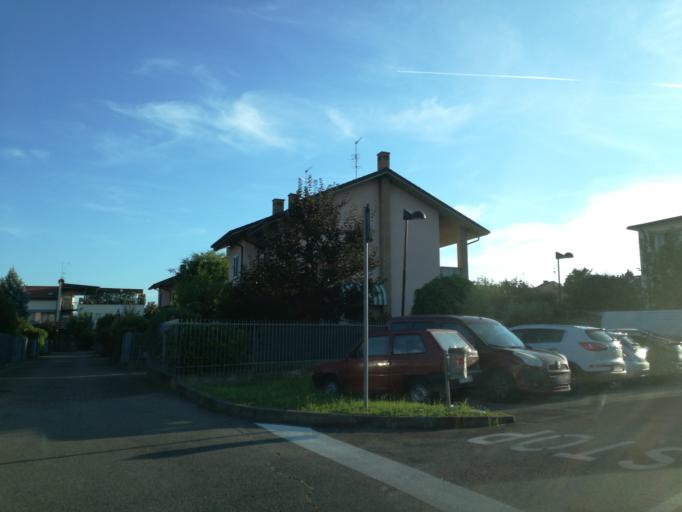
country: IT
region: Lombardy
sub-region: Provincia di Monza e Brianza
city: Sulbiate
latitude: 45.6398
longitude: 9.4256
